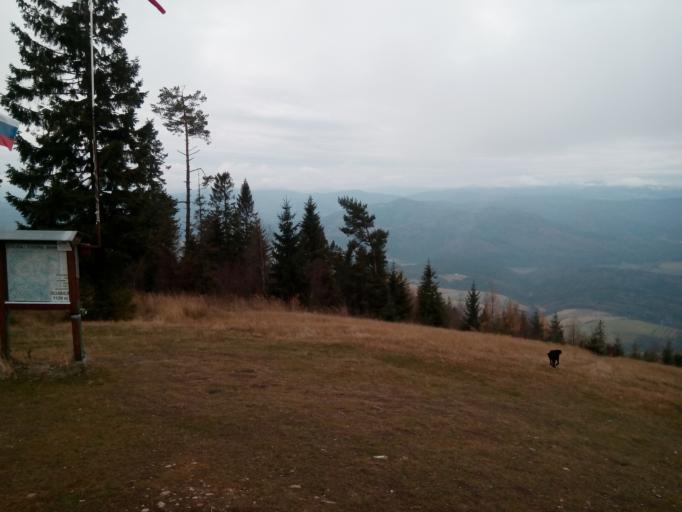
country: SK
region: Kosicky
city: Krompachy
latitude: 48.9734
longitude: 20.8722
